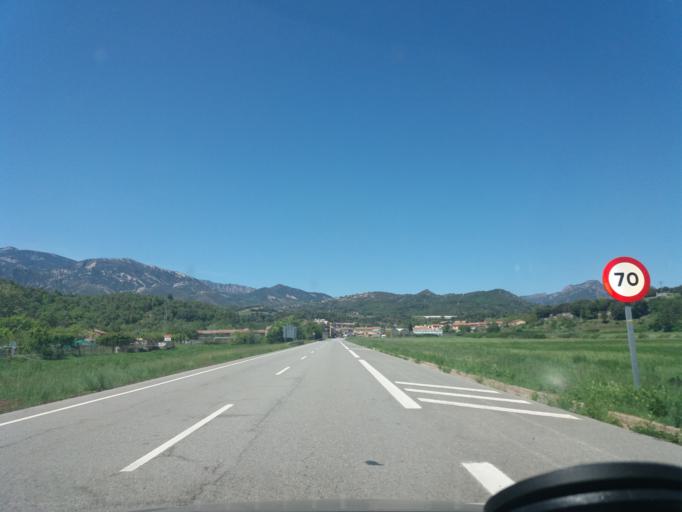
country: ES
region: Catalonia
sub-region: Provincia de Barcelona
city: Avia
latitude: 42.0652
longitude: 1.8708
